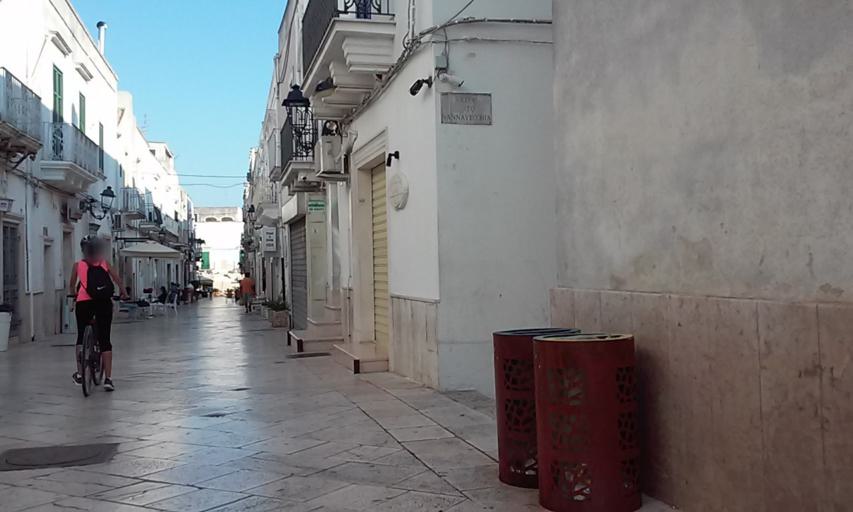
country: IT
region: Apulia
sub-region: Provincia di Brindisi
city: Ceglie Messapica
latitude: 40.6470
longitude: 17.5161
